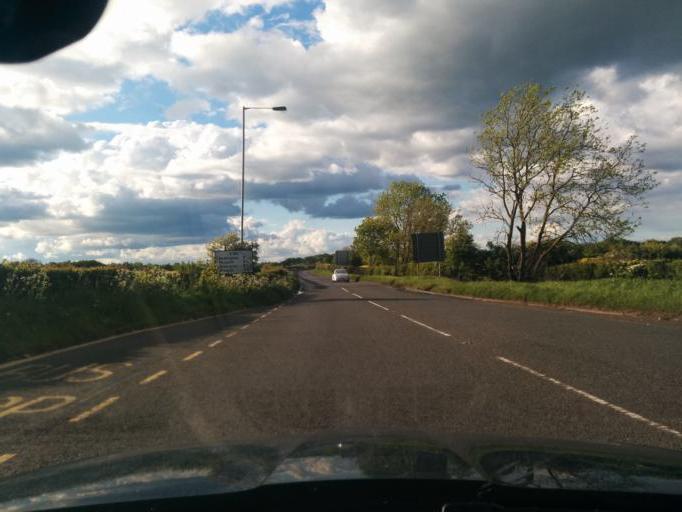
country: GB
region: England
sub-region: Northumberland
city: Bedlington
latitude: 55.1059
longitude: -1.6180
